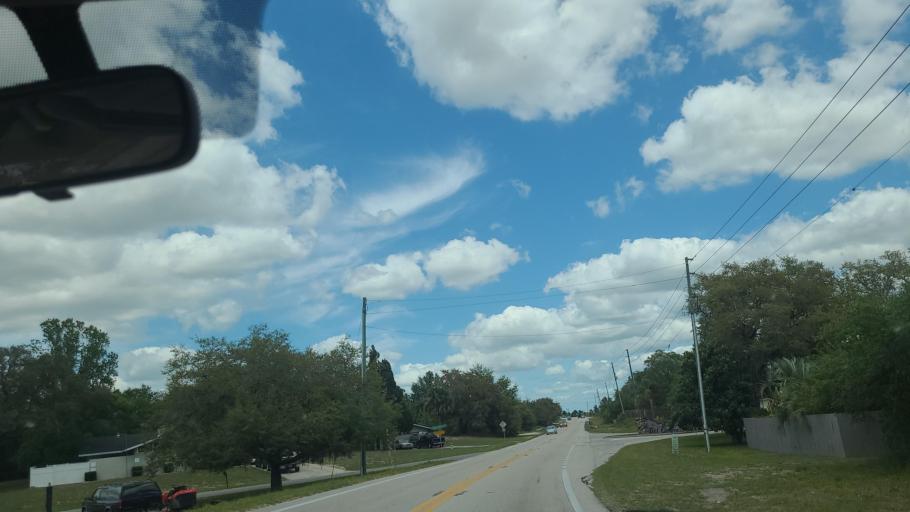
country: US
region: Florida
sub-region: Polk County
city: Lake Wales
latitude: 27.9090
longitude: -81.5559
